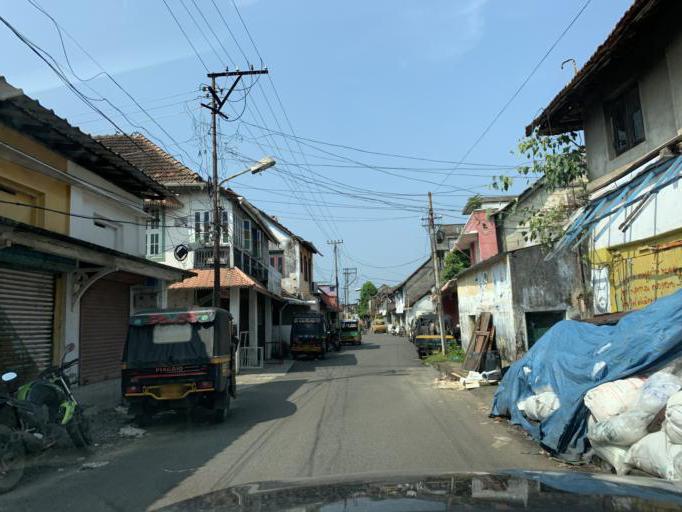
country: IN
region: Kerala
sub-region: Ernakulam
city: Cochin
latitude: 9.9526
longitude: 76.2606
